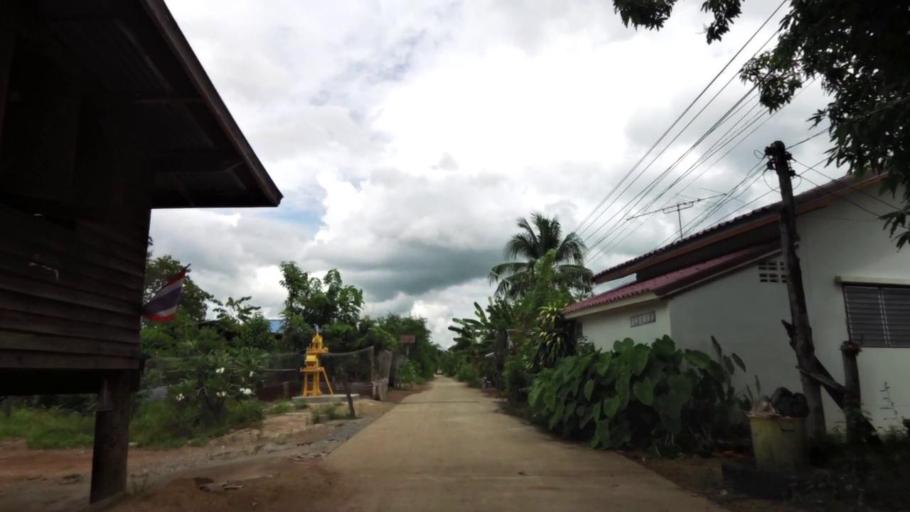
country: TH
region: Nakhon Sawan
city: Phai Sali
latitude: 15.6005
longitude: 100.6549
